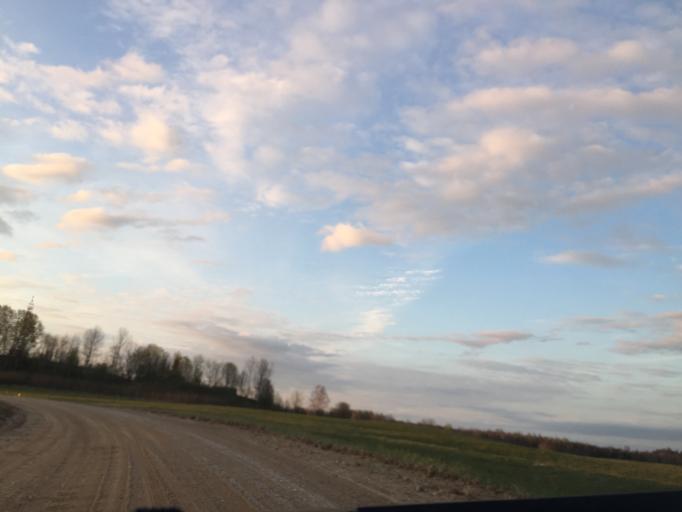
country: LV
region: Gulbenes Rajons
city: Gulbene
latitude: 57.2183
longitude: 26.7885
